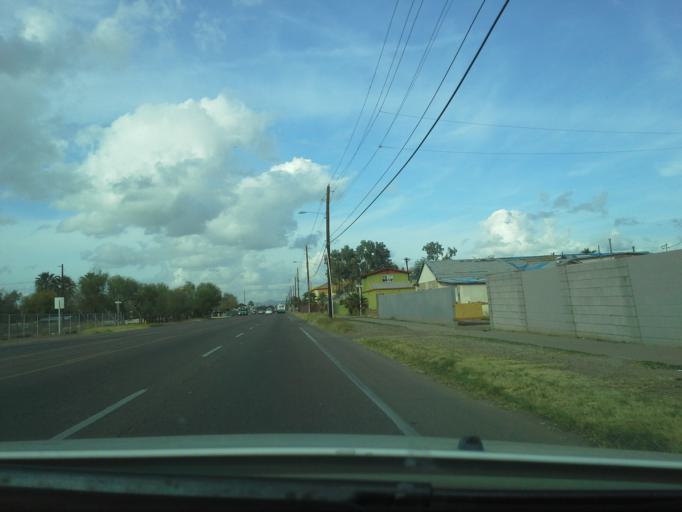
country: US
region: Arizona
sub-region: Maricopa County
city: Phoenix
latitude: 33.4017
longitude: -112.0819
